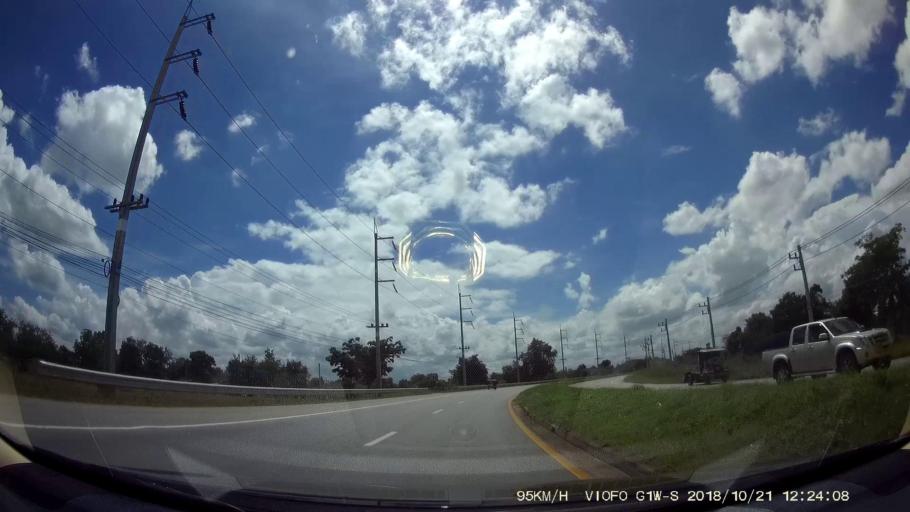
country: TH
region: Nakhon Ratchasima
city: Dan Khun Thot
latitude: 15.2361
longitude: 101.7870
